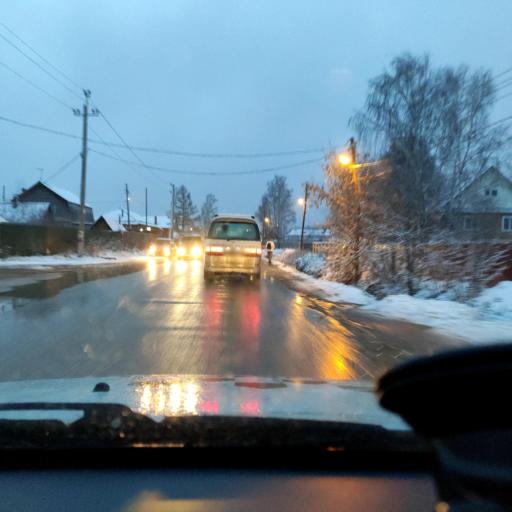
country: RU
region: Perm
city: Kondratovo
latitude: 58.0487
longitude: 56.0305
